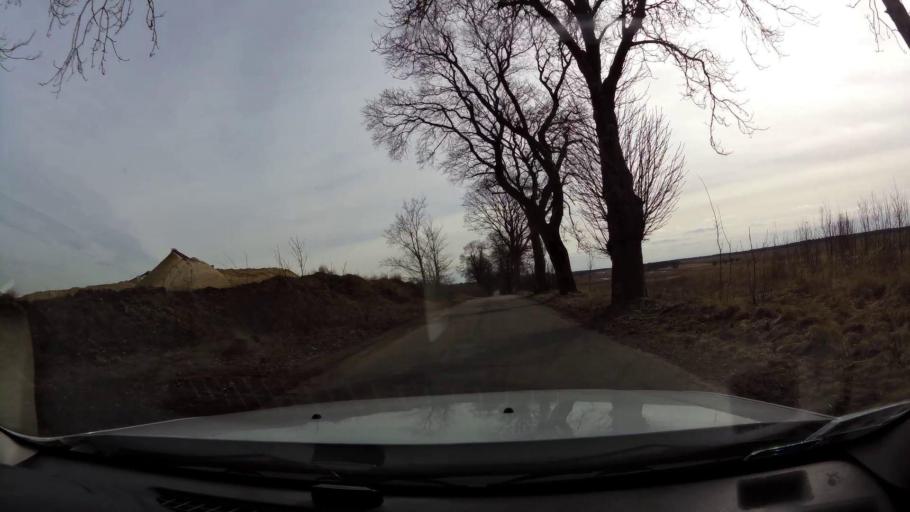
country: PL
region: West Pomeranian Voivodeship
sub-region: Powiat stargardzki
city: Insko
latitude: 53.4670
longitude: 15.5982
